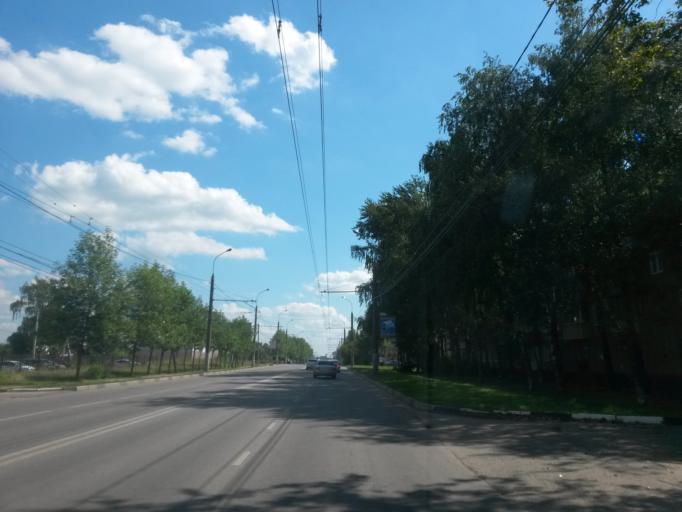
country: RU
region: Ivanovo
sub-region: Gorod Ivanovo
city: Ivanovo
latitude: 56.9732
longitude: 41.0102
